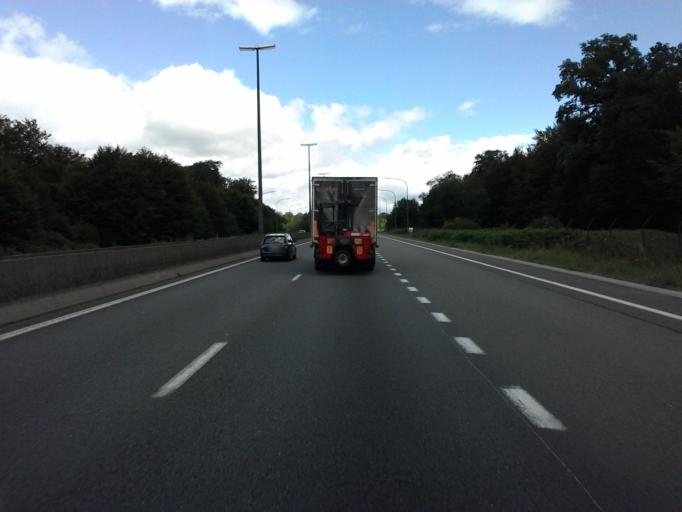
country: BE
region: Wallonia
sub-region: Province du Luxembourg
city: Habay-la-Vieille
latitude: 49.7431
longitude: 5.5725
